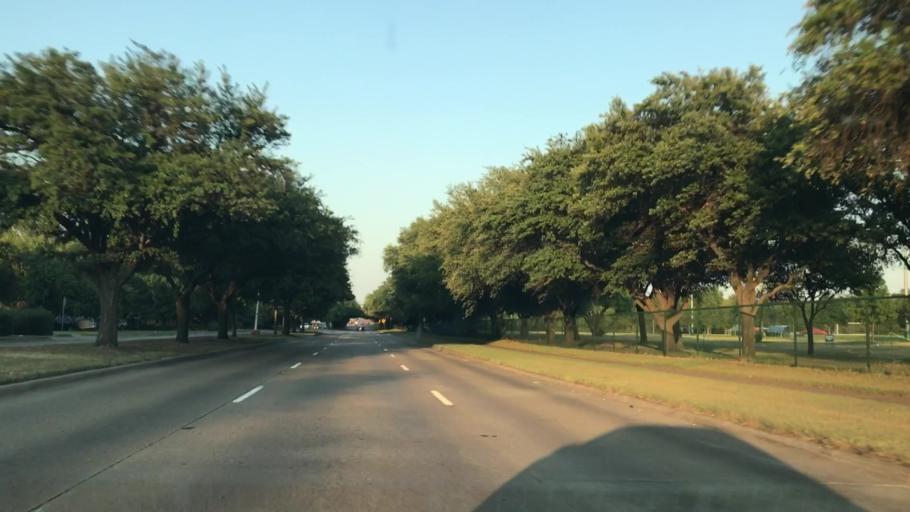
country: US
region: Texas
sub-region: Dallas County
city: Addison
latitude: 32.9094
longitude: -96.8239
